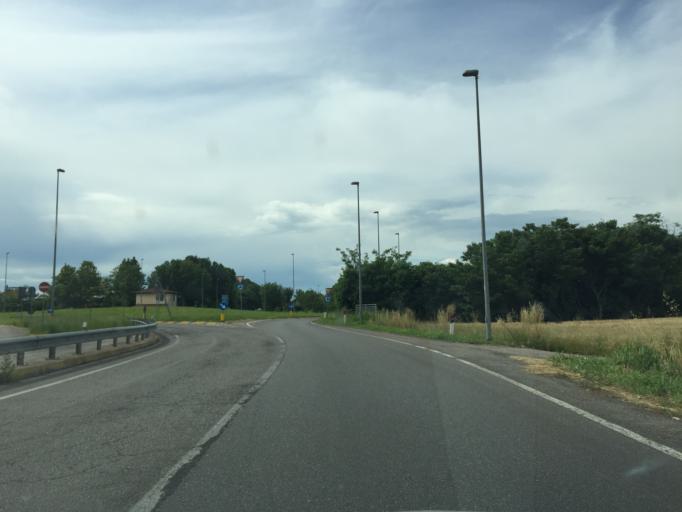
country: IT
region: Lombardy
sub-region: Provincia di Brescia
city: Ghedi
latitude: 45.4195
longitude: 10.2612
